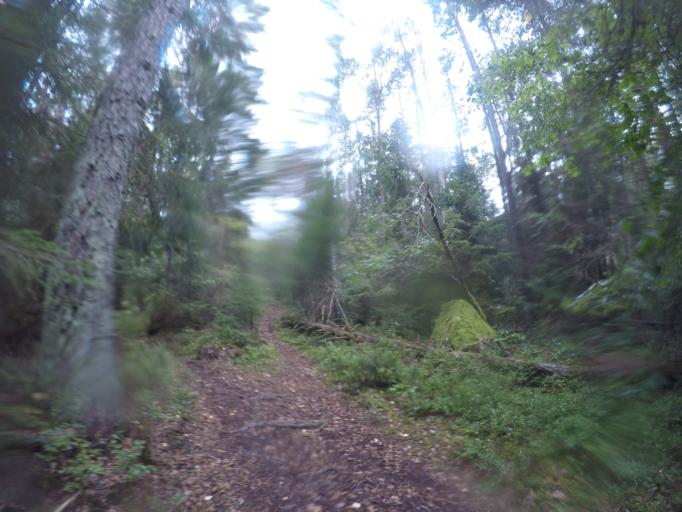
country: SE
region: Vaestmanland
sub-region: Vasteras
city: Vasteras
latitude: 59.6464
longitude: 16.5172
